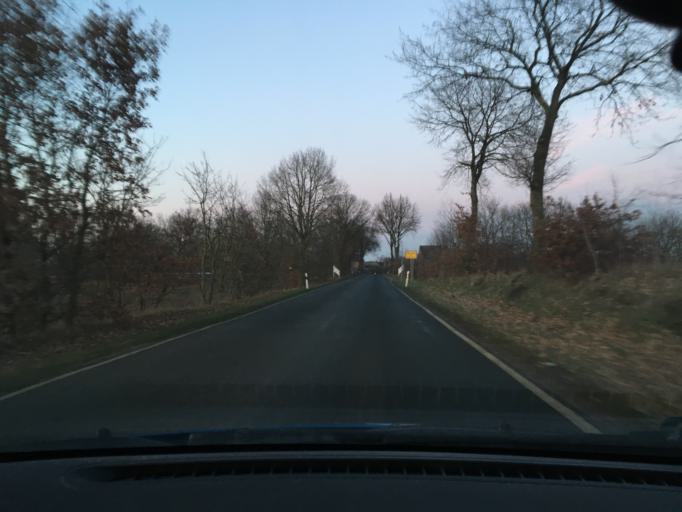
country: DE
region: Schleswig-Holstein
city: Fitzen
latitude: 53.4912
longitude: 10.6446
